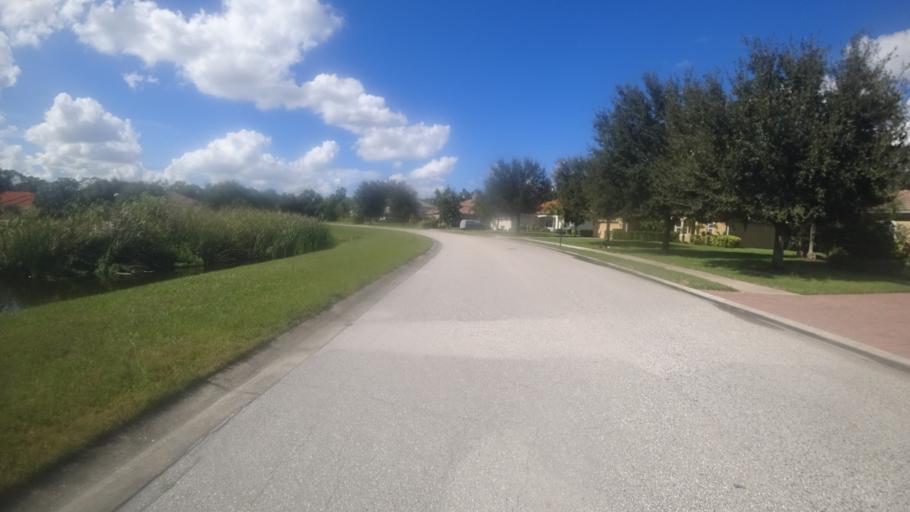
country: US
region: Florida
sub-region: Manatee County
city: Ellenton
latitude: 27.5013
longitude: -82.3951
